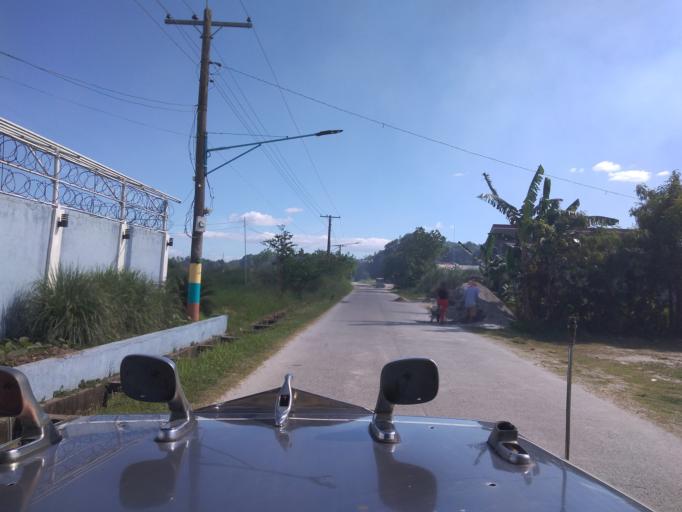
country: PH
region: Central Luzon
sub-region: Province of Pampanga
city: Magliman
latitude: 15.0297
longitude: 120.6351
